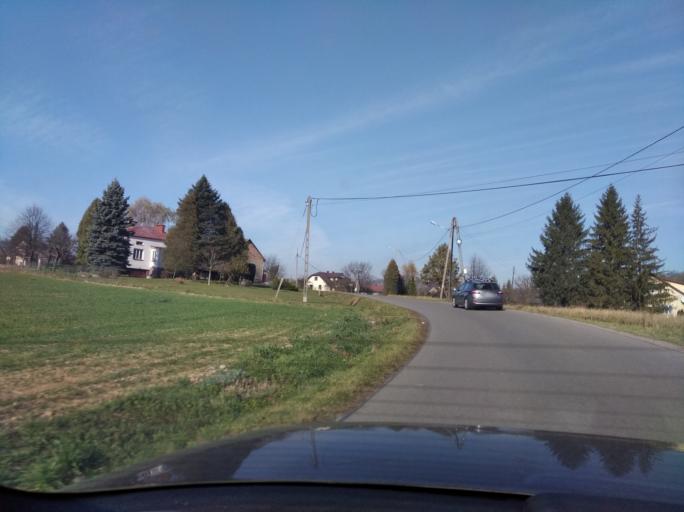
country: PL
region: Subcarpathian Voivodeship
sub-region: Powiat strzyzowski
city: Wisniowa
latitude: 49.8672
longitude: 21.6402
